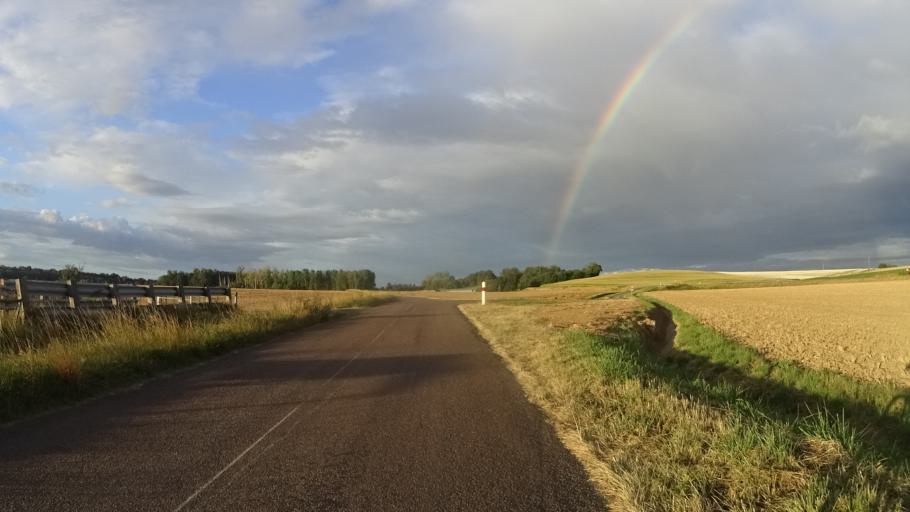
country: FR
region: Bourgogne
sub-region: Departement de Saone-et-Loire
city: Verdun-sur-le-Doubs
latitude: 46.9550
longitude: 5.0688
